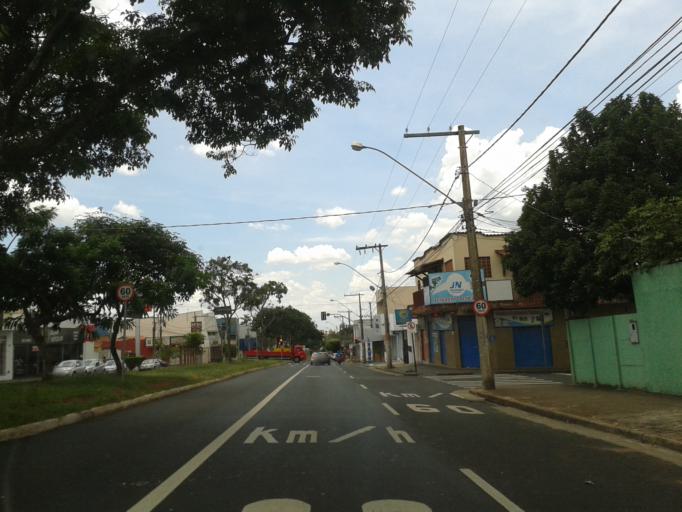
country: BR
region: Minas Gerais
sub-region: Uberlandia
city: Uberlandia
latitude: -18.9187
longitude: -48.2476
